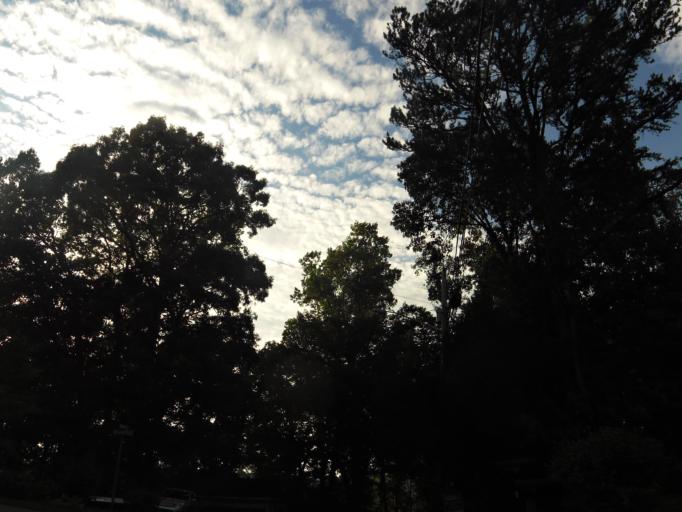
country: US
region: Tennessee
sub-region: Knox County
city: Knoxville
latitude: 36.0439
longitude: -83.9469
